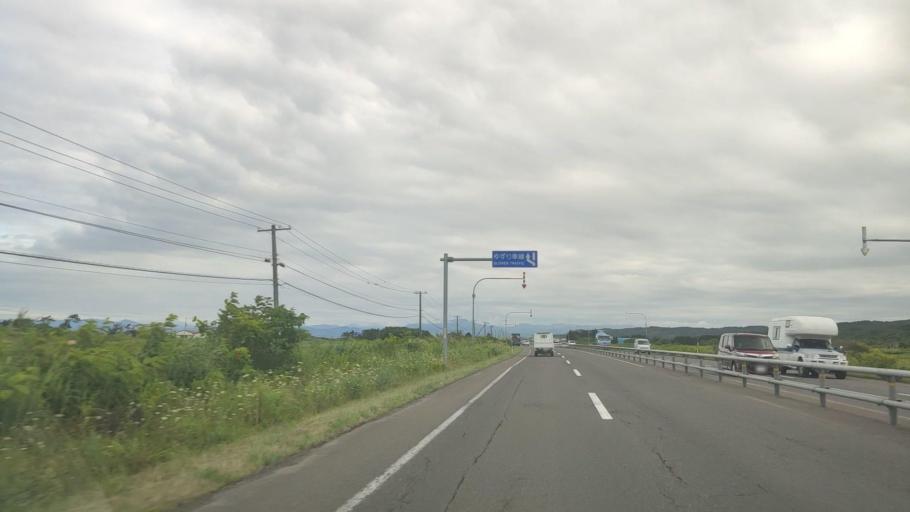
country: JP
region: Hokkaido
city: Niseko Town
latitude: 42.4108
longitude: 140.3071
